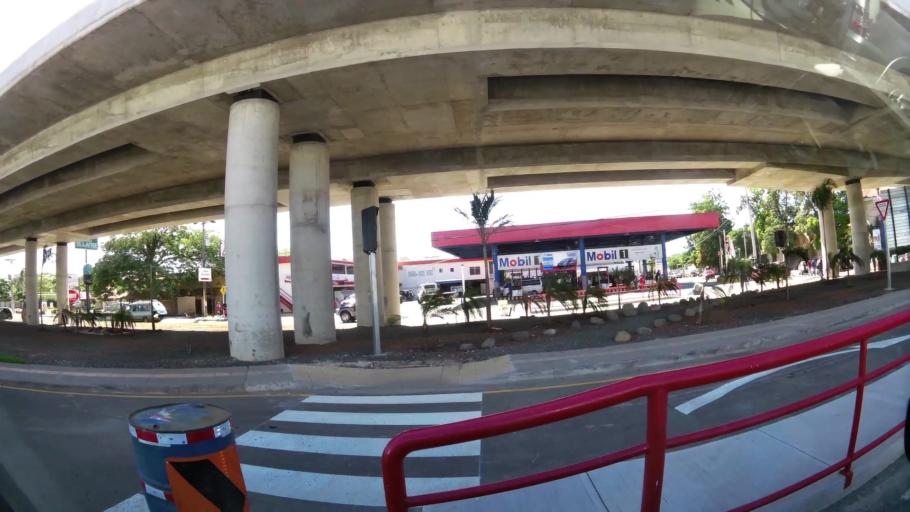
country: CR
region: Guanacaste
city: Liberia
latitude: 10.6266
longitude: -85.4434
